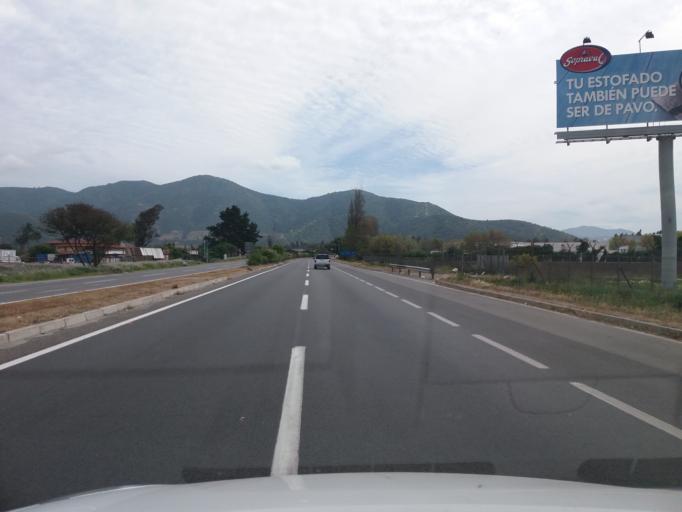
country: CL
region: Valparaiso
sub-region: Provincia de Quillota
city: Hacienda La Calera
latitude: -32.7698
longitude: -71.1905
